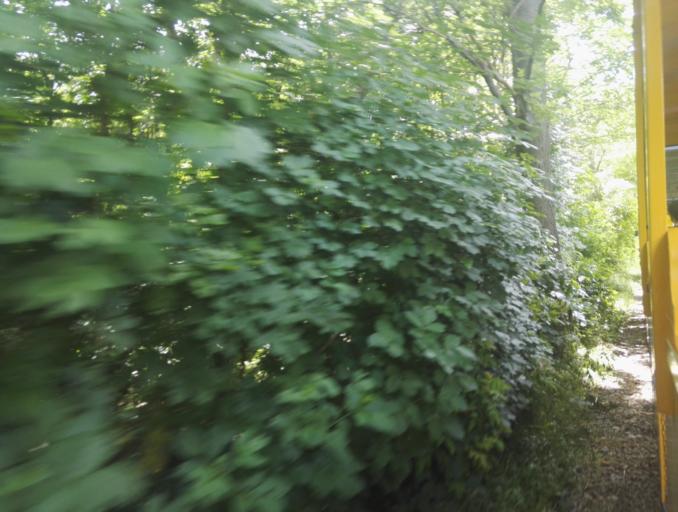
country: AT
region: Vienna
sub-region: Wien Stadt
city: Vienna
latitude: 48.2383
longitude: 16.4065
